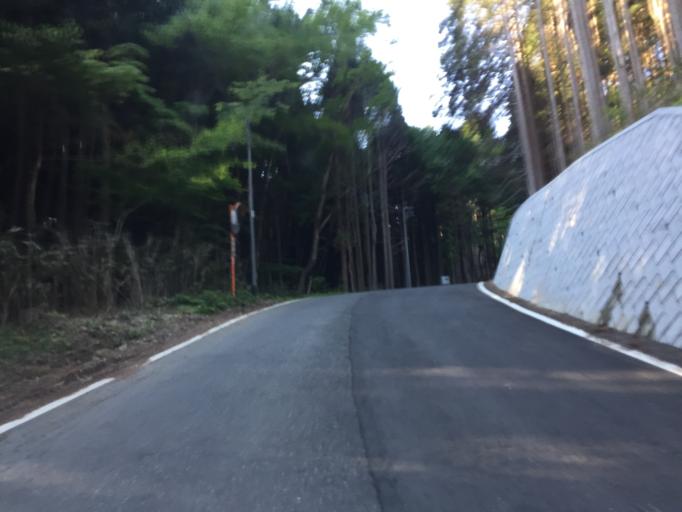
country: JP
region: Ibaraki
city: Kitaibaraki
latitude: 36.8975
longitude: 140.6198
